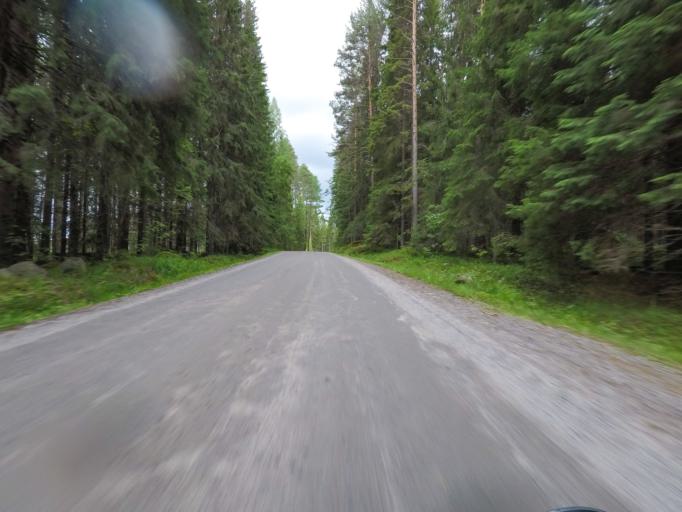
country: FI
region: Central Finland
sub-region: Jyvaeskylae
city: Hankasalmi
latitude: 62.4137
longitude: 26.6139
